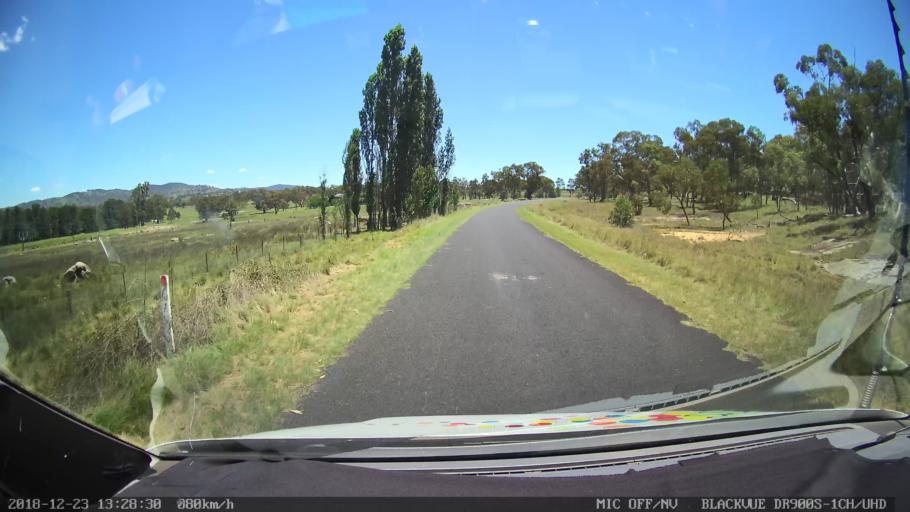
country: AU
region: New South Wales
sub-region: Armidale Dumaresq
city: Armidale
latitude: -30.4671
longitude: 151.3481
